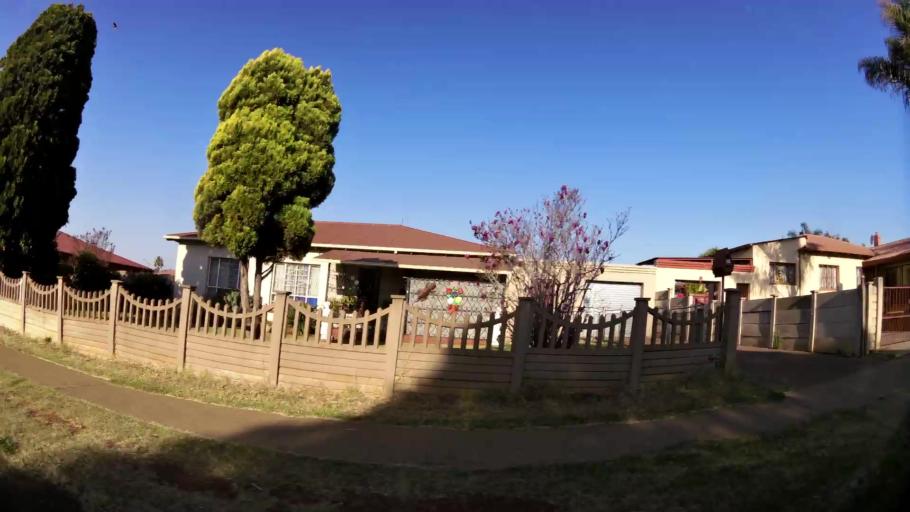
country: ZA
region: Gauteng
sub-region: City of Tshwane Metropolitan Municipality
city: Pretoria
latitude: -25.7528
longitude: 28.1302
